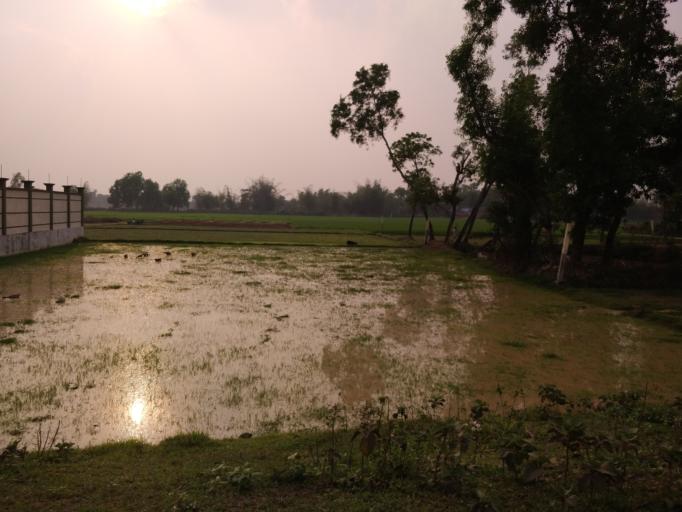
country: BD
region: Sylhet
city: Habiganj
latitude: 24.1443
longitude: 91.3511
